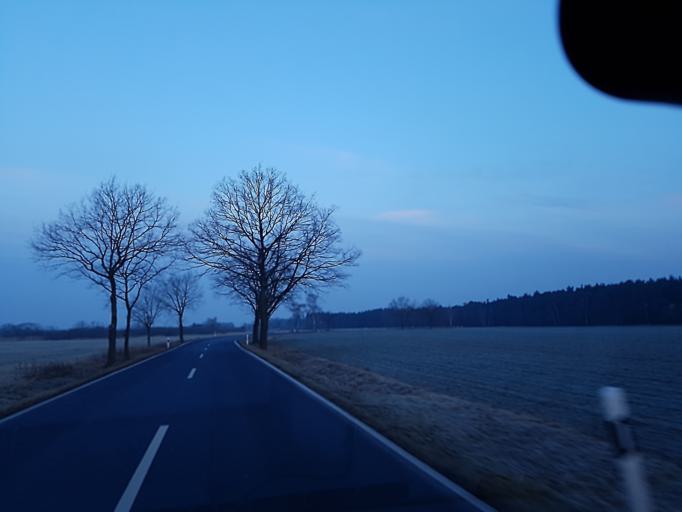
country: DE
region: Saxony-Anhalt
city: Holzdorf
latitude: 51.7528
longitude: 13.1417
